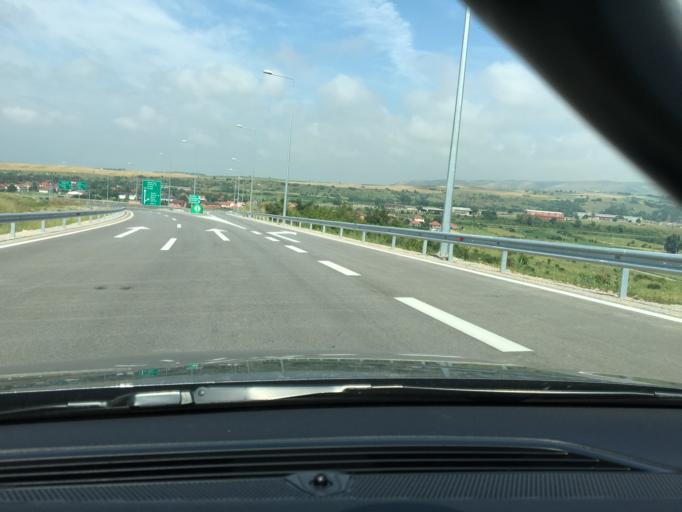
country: MK
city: Miladinovci
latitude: 41.9879
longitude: 21.6617
